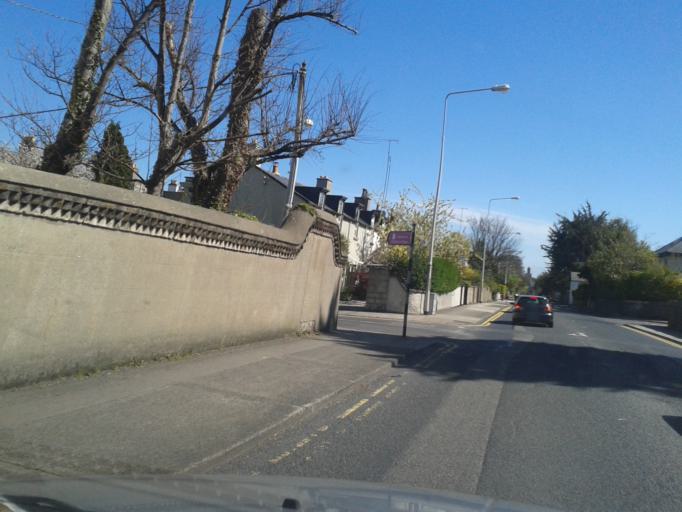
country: IE
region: Leinster
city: Monkstown
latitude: 53.2951
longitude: -6.1637
